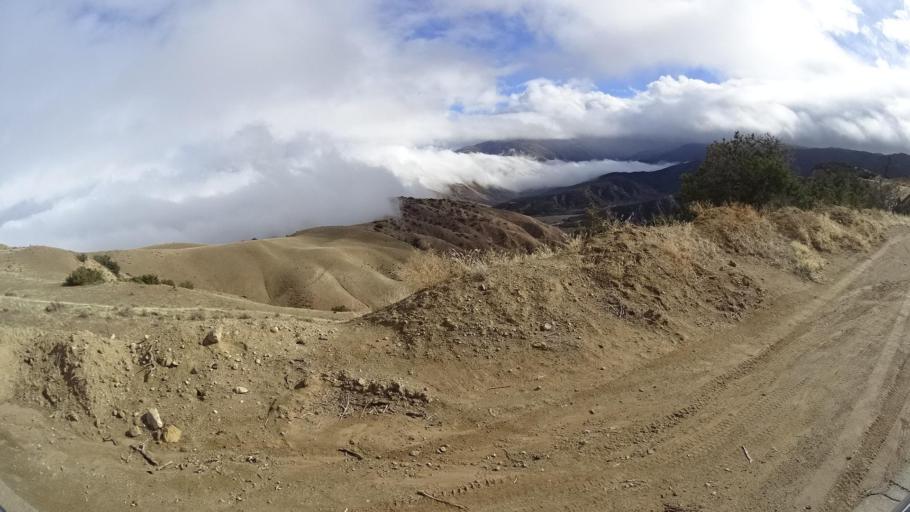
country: US
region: California
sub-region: Kern County
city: Maricopa
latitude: 34.8965
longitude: -119.3661
